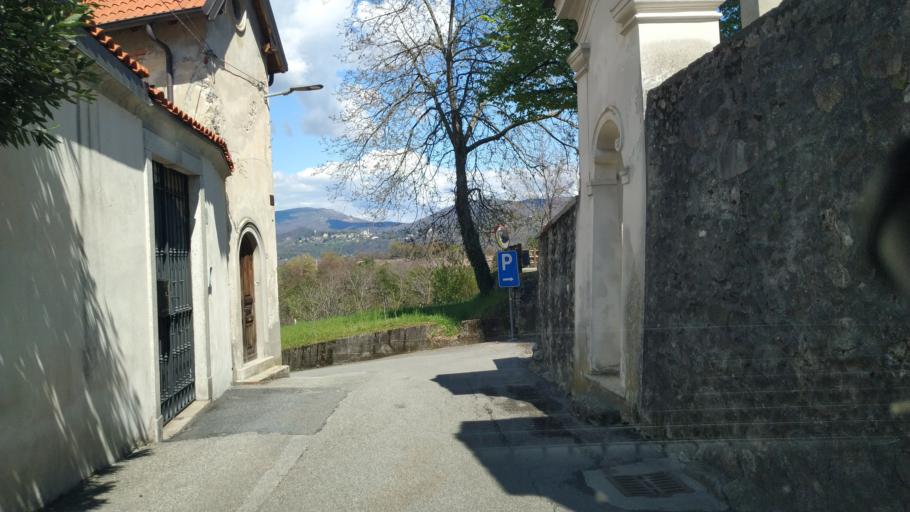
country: IT
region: Piedmont
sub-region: Provincia di Novara
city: San Maurizio D'Opaglio
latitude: 45.7764
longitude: 8.3896
